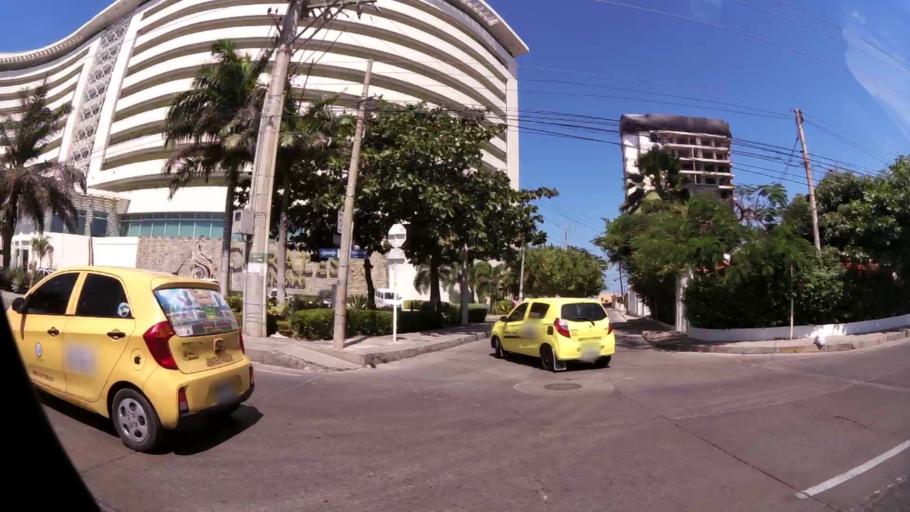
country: CO
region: Bolivar
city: Cartagena
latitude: 10.4429
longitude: -75.5249
